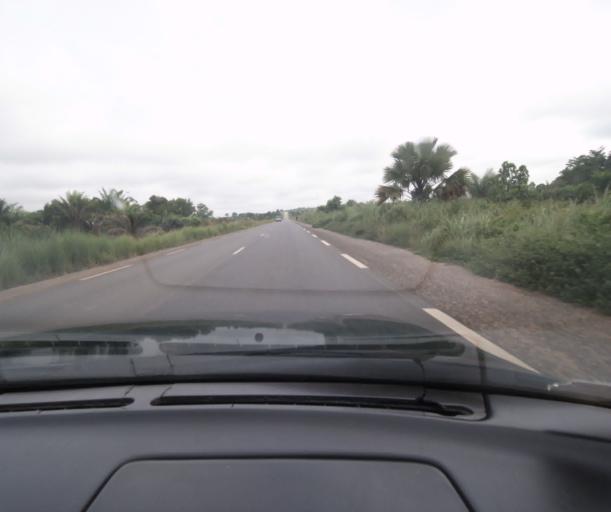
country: CM
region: Centre
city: Saa
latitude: 4.3918
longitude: 11.2537
